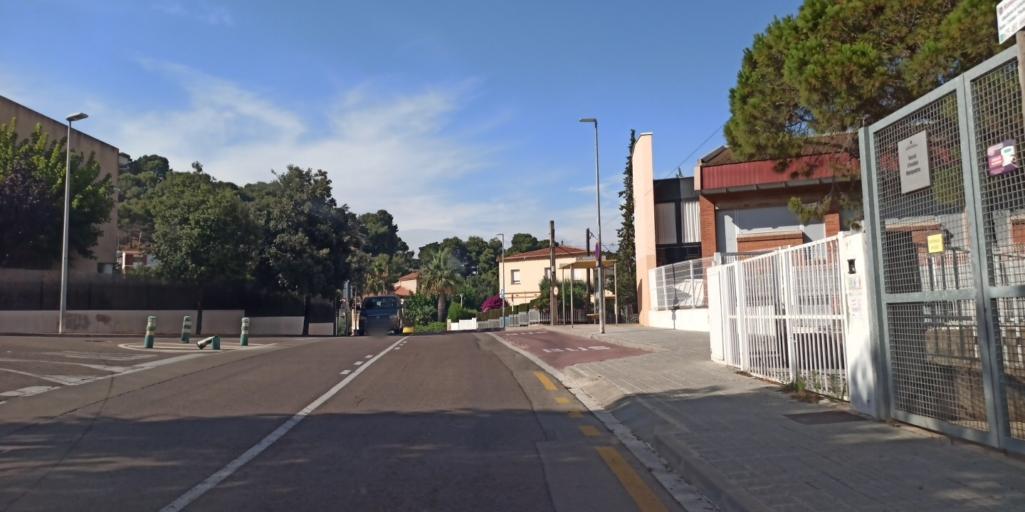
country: ES
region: Catalonia
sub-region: Provincia de Barcelona
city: Santa Coloma de Cervello
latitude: 41.3646
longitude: 2.0125
